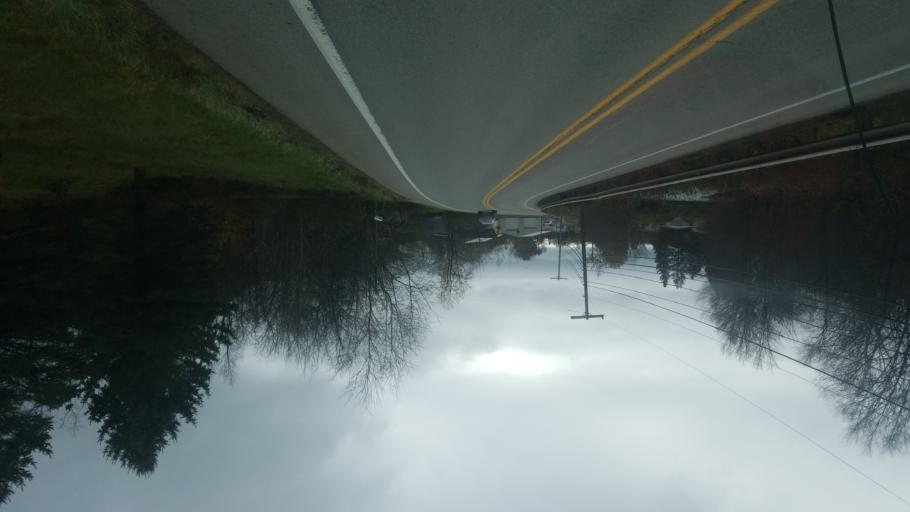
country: US
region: Pennsylvania
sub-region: Jefferson County
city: Brockway
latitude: 41.2620
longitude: -78.7237
